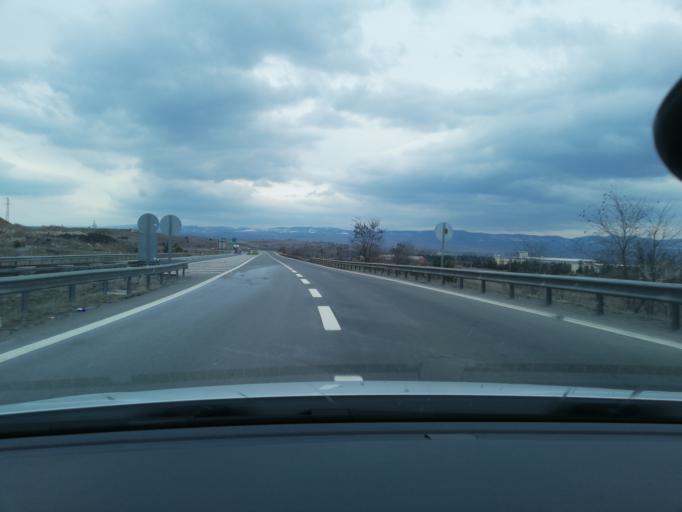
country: TR
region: Bolu
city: Gerede
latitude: 40.7768
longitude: 32.2124
